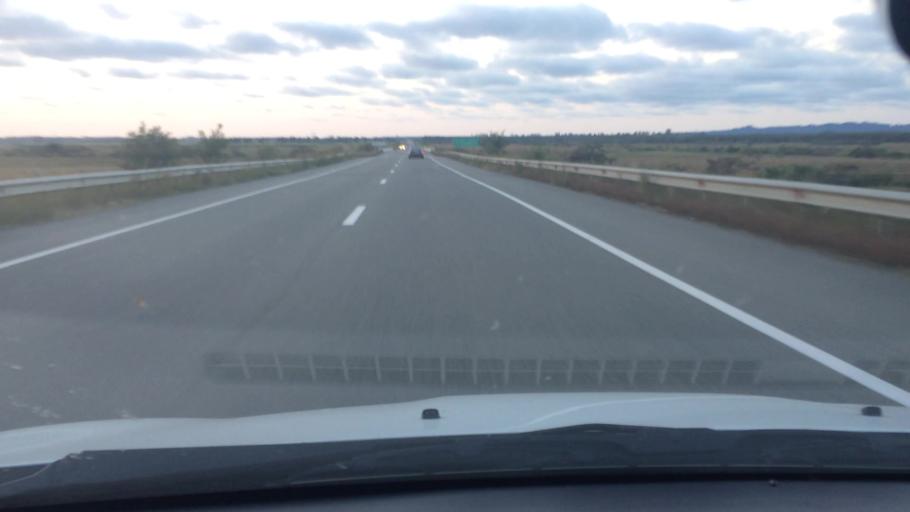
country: GE
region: Ajaria
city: Ochkhamuri
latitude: 41.8697
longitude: 41.8325
